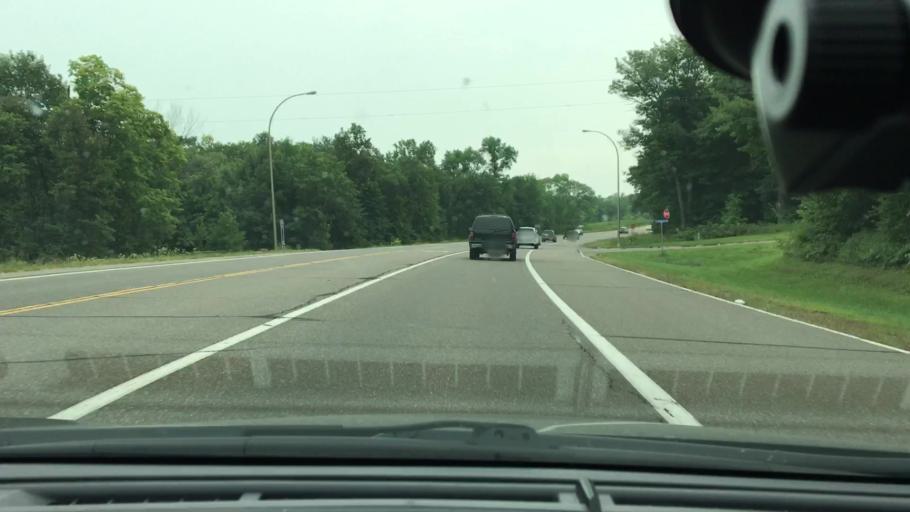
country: US
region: Minnesota
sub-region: Mille Lacs County
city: Vineland
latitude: 46.2003
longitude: -93.7663
